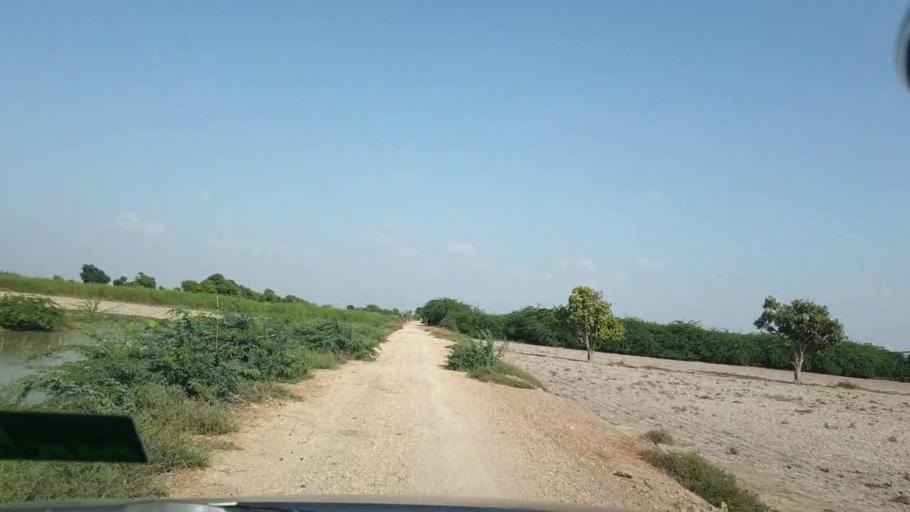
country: PK
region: Sindh
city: Naukot
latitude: 24.7030
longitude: 69.2265
